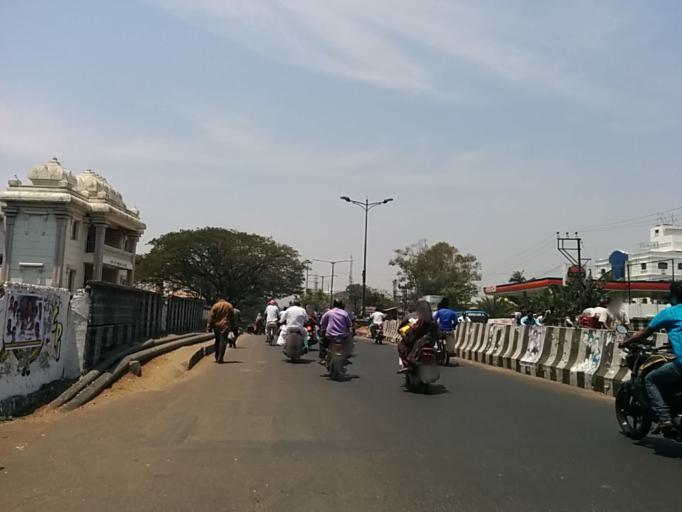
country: IN
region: Pondicherry
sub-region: Puducherry
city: Puducherry
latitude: 11.9306
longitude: 79.8222
